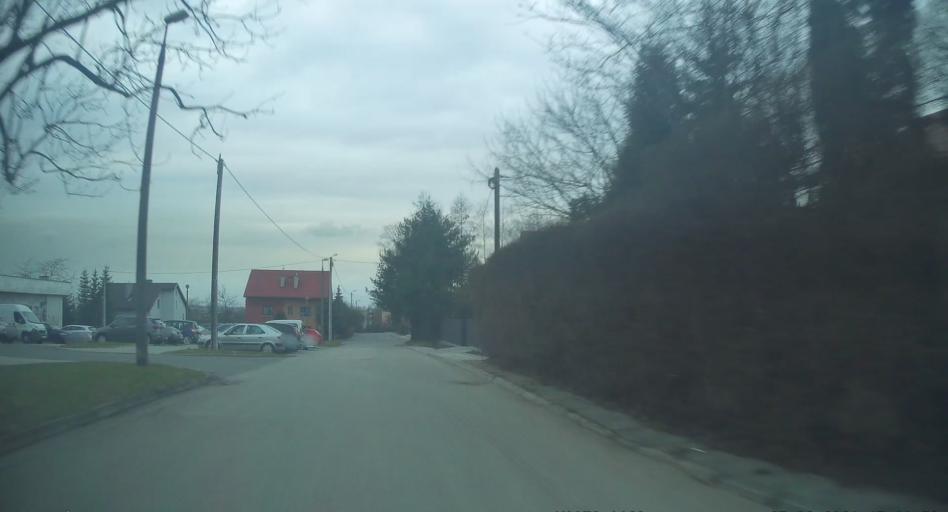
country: PL
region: Lesser Poland Voivodeship
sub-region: Krakow
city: Krakow
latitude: 50.0150
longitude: 19.9603
